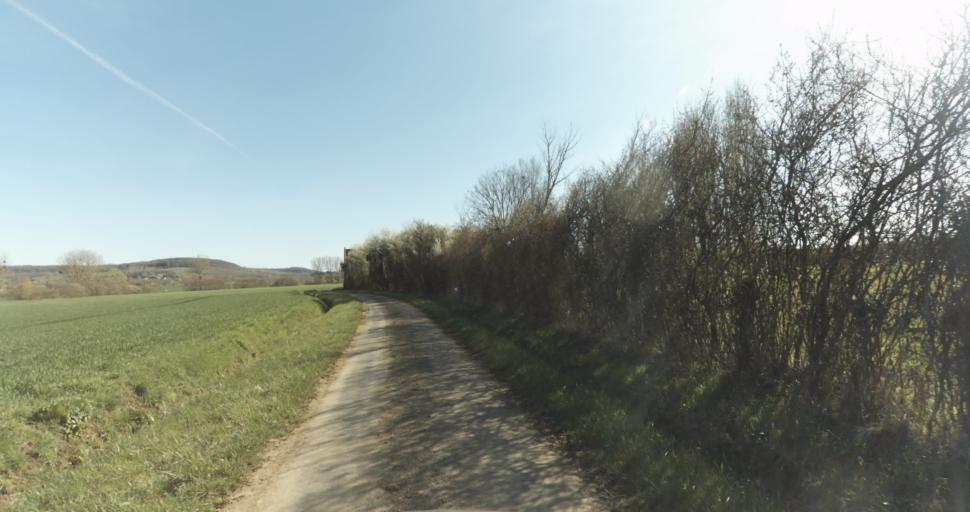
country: FR
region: Lower Normandy
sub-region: Departement du Calvados
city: Saint-Pierre-sur-Dives
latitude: 49.0291
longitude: 0.0197
